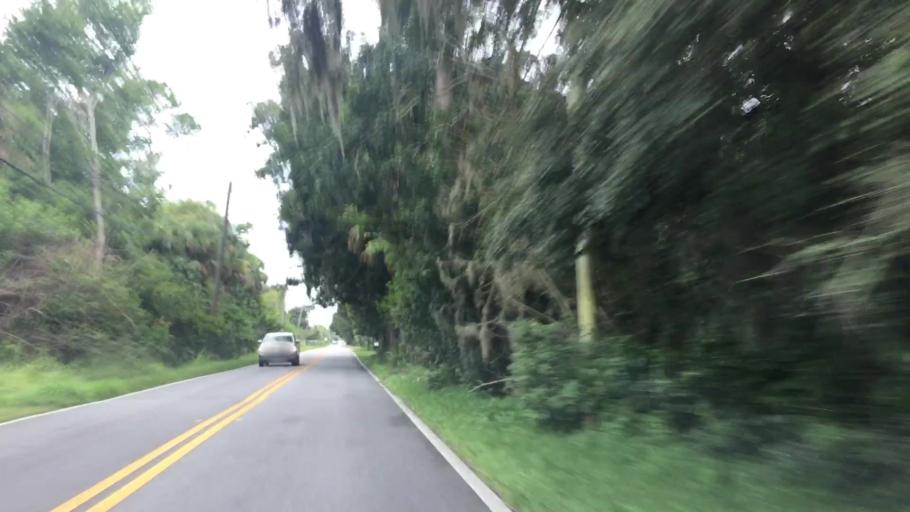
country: US
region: Florida
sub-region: Seminole County
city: Midway
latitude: 28.8014
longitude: -81.2186
